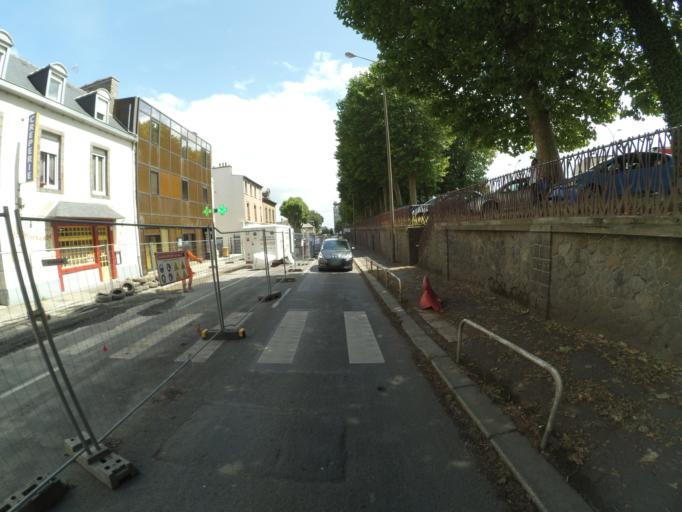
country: FR
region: Brittany
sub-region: Departement des Cotes-d'Armor
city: Saint-Brieuc
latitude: 48.5078
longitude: -2.7634
